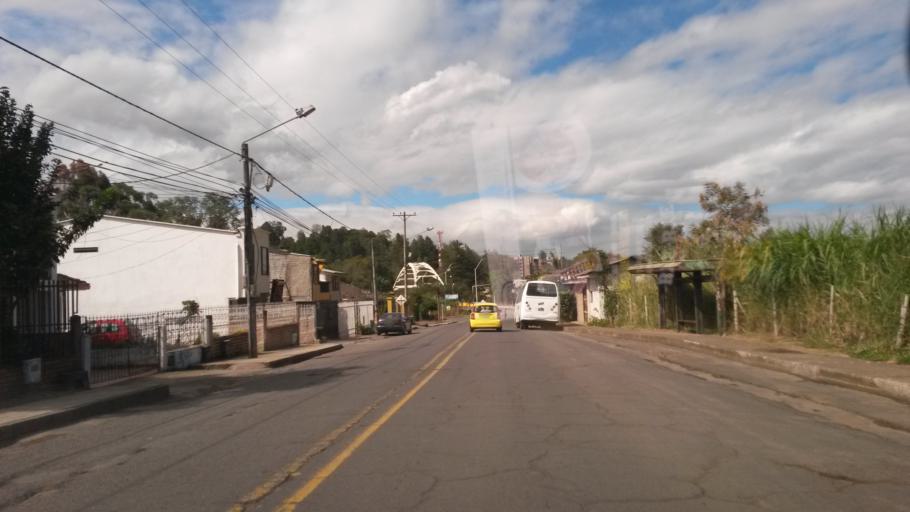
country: CO
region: Cauca
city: Popayan
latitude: 2.4724
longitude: -76.5780
